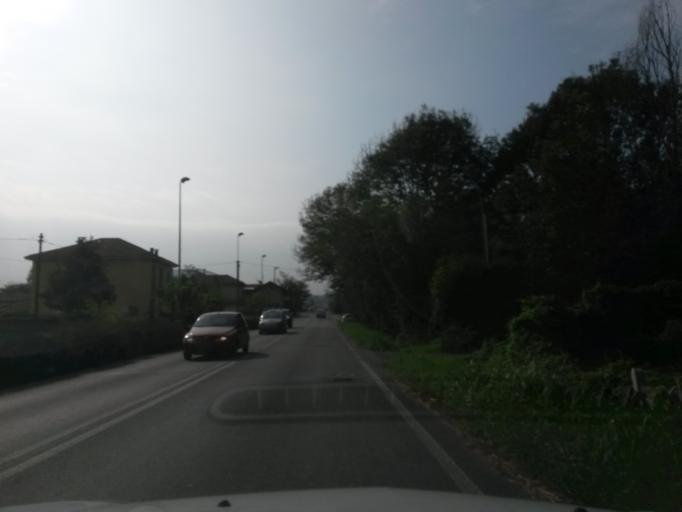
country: IT
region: Piedmont
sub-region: Provincia di Torino
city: Avigliana
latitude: 45.0919
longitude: 7.4033
